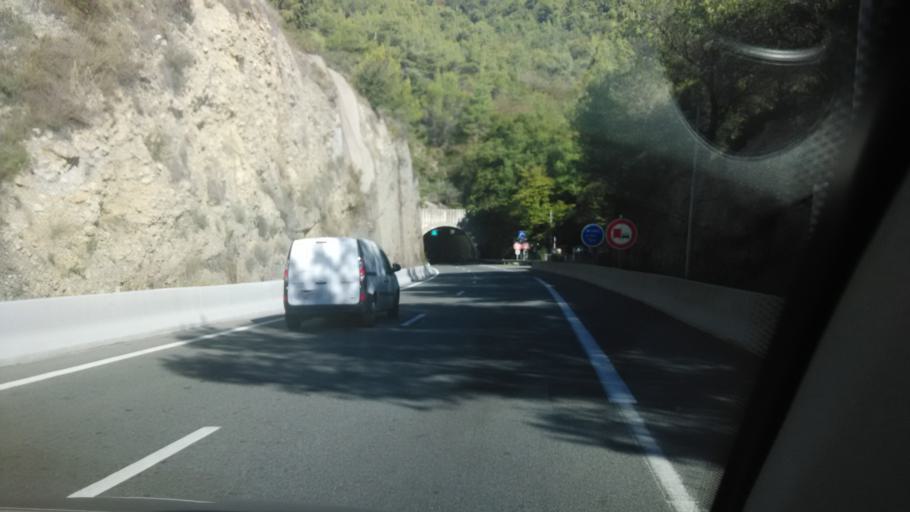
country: FR
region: Provence-Alpes-Cote d'Azur
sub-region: Departement des Alpes-Maritimes
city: Gorbio
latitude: 43.7704
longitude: 7.4498
